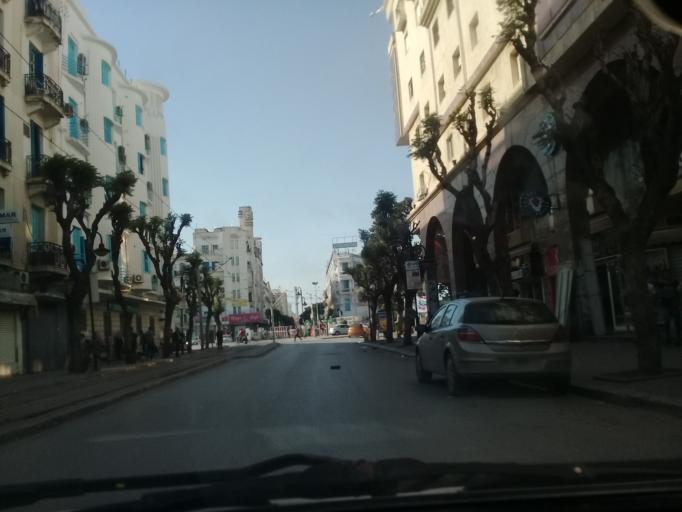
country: TN
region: Tunis
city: Tunis
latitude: 36.8049
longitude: 10.1807
